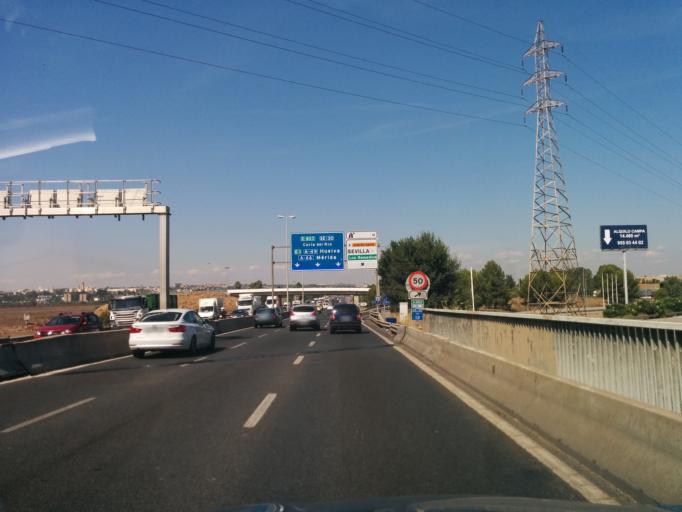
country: ES
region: Andalusia
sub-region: Provincia de Sevilla
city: Gelves
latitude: 37.3570
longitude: -6.0025
